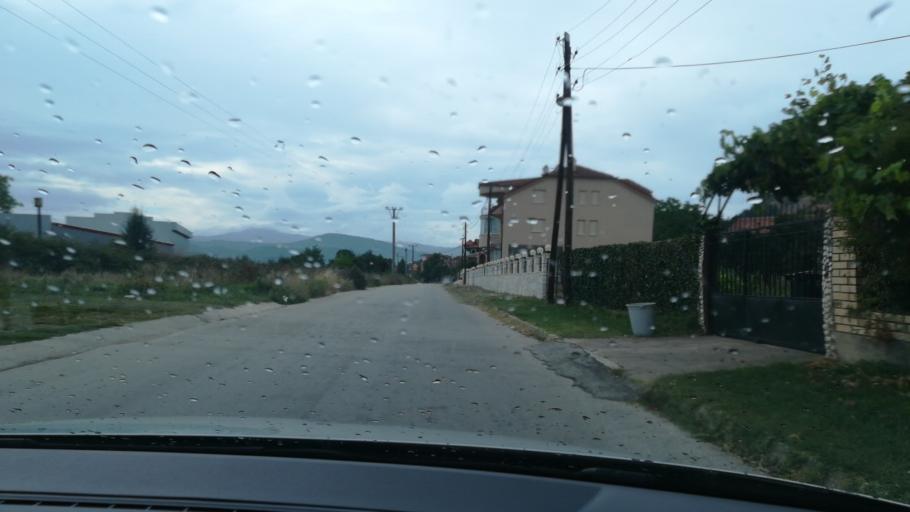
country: MK
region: Kicevo
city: Kicevo
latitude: 41.5196
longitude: 20.9513
